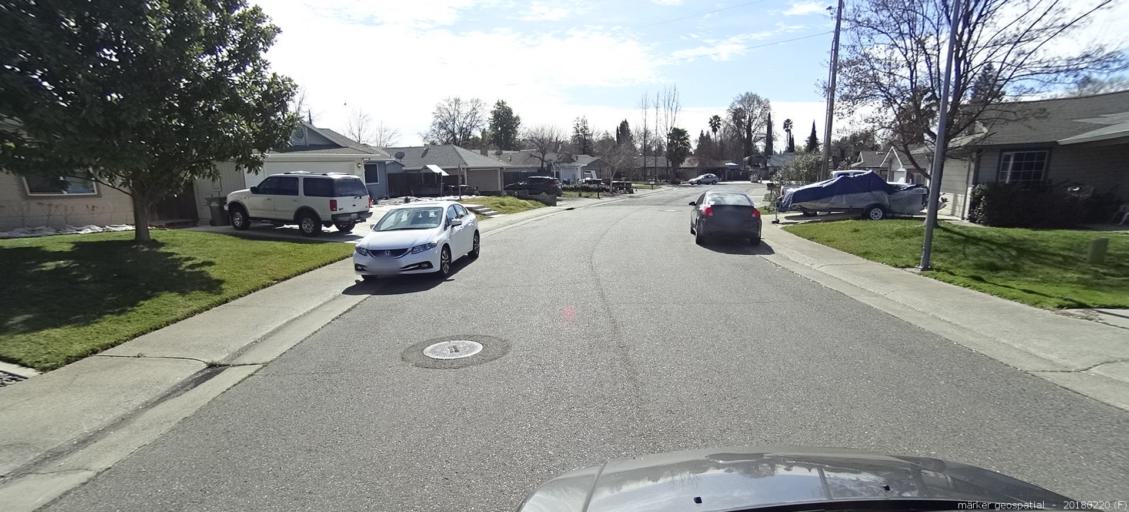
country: US
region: California
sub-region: Sacramento County
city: Orangevale
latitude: 38.6731
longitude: -121.2146
